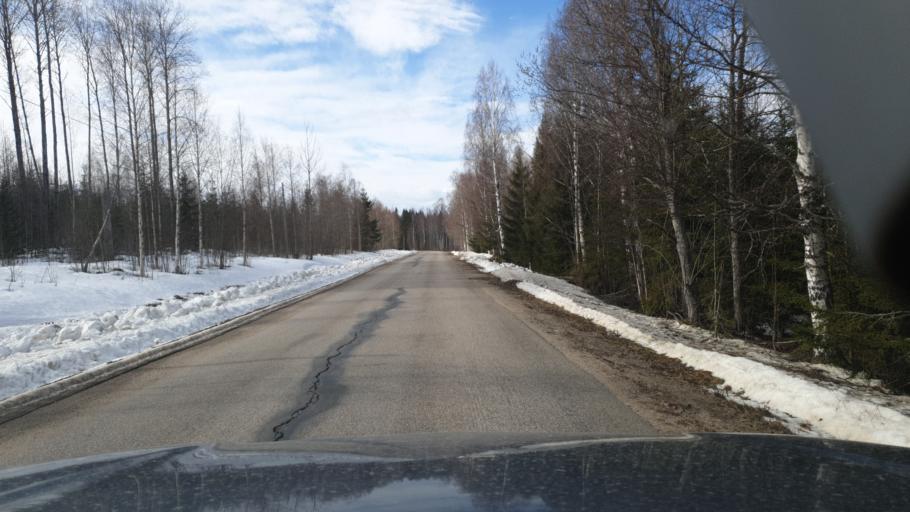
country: SE
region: Gaevleborg
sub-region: Ljusdals Kommun
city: Farila
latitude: 61.8429
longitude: 15.8909
